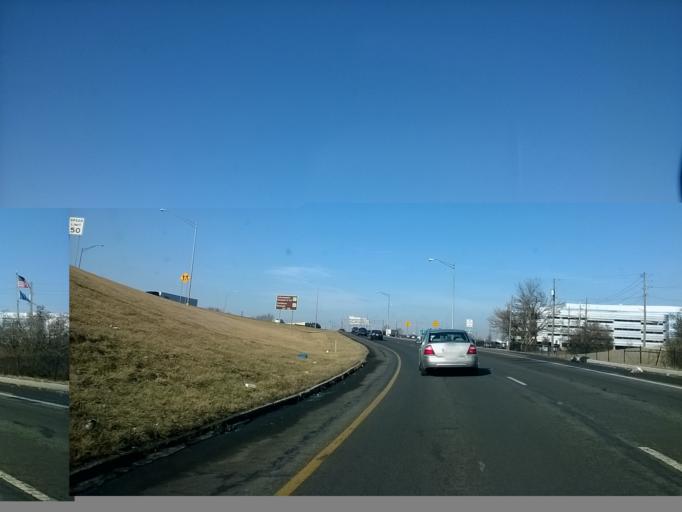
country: US
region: Indiana
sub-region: Marion County
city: Indianapolis
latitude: 39.7849
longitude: -86.1658
